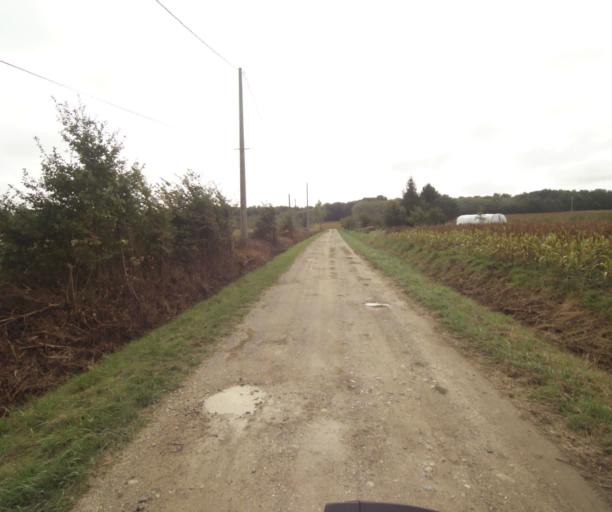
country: FR
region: Midi-Pyrenees
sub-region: Departement du Tarn-et-Garonne
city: Campsas
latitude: 43.9191
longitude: 1.2971
